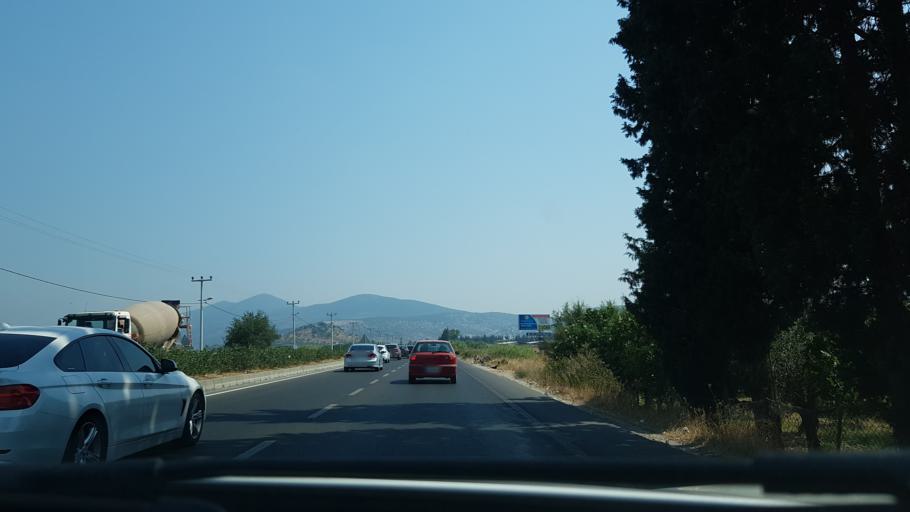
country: TR
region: Mugla
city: Milas
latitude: 37.2425
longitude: 27.7162
